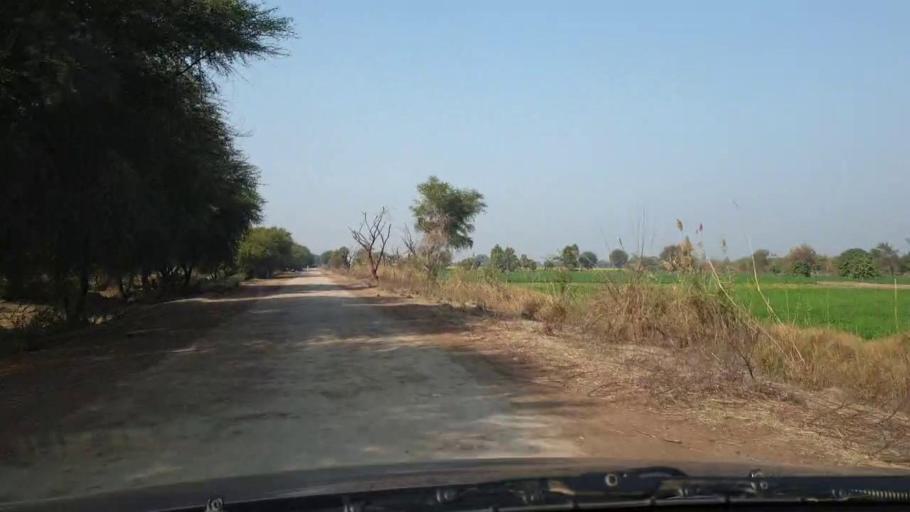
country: PK
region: Sindh
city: Jhol
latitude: 25.9614
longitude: 68.9684
